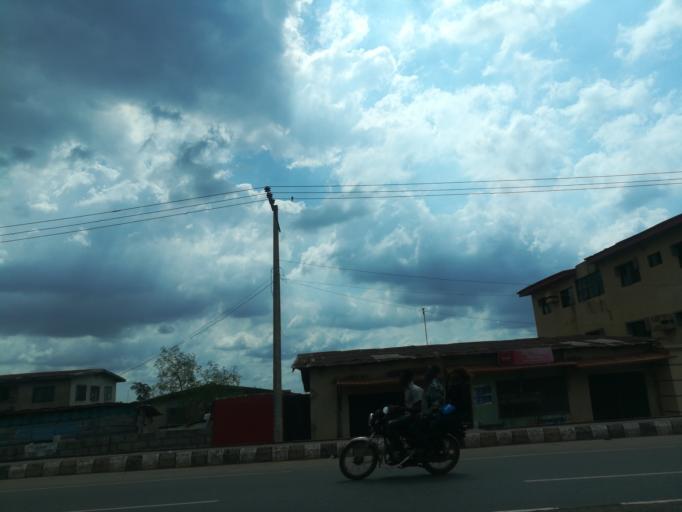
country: NG
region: Oyo
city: Ibadan
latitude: 7.4159
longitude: 3.8624
